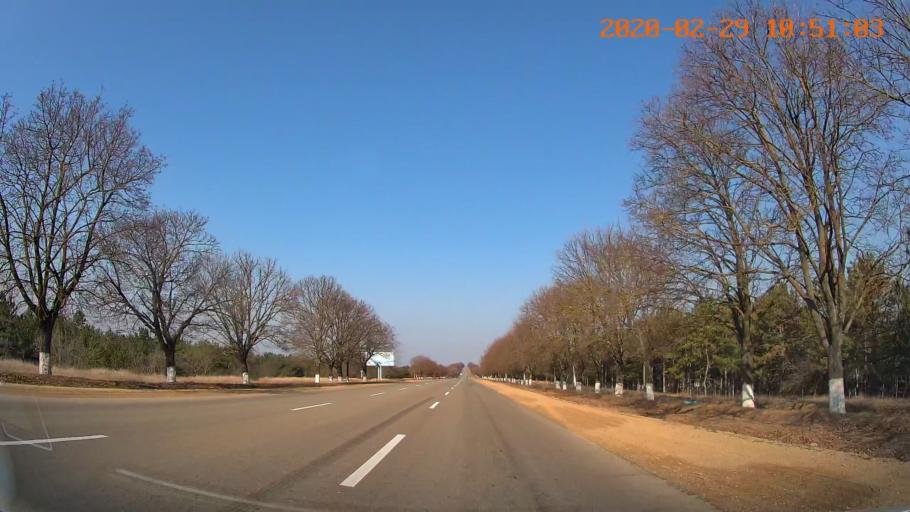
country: MD
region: Telenesti
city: Grigoriopol
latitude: 47.0891
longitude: 29.3693
